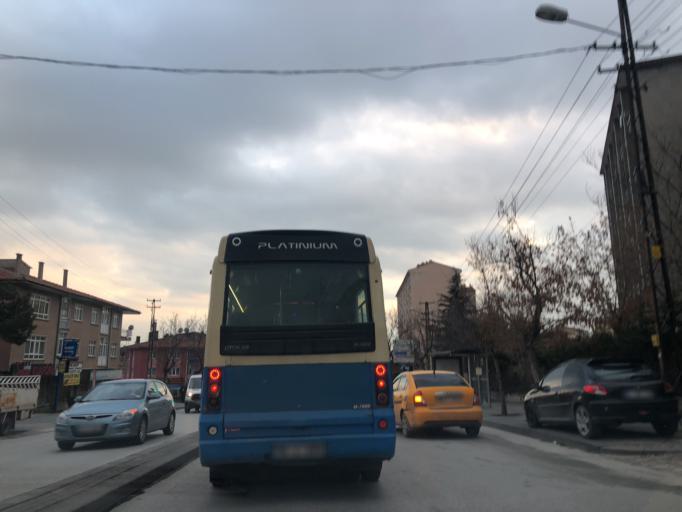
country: TR
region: Ankara
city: Ankara
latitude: 39.9726
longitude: 32.8111
